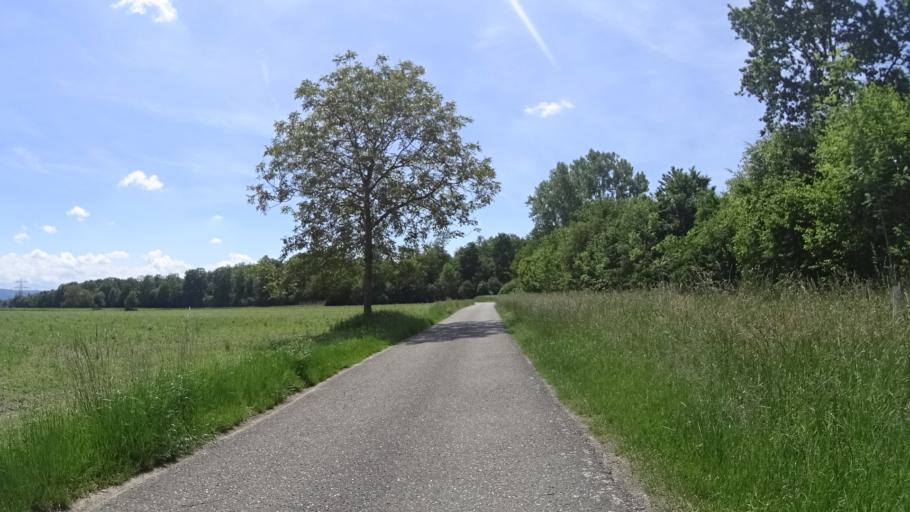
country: DE
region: Baden-Wuerttemberg
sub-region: Freiburg Region
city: Grafenhausen
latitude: 48.3196
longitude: 7.7506
